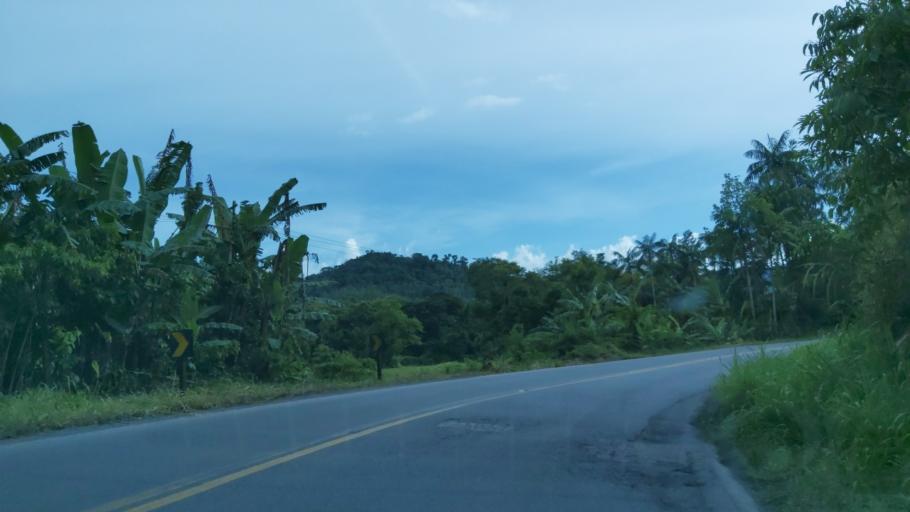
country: BR
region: Sao Paulo
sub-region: Miracatu
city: Miracatu
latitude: -24.0663
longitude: -47.5968
